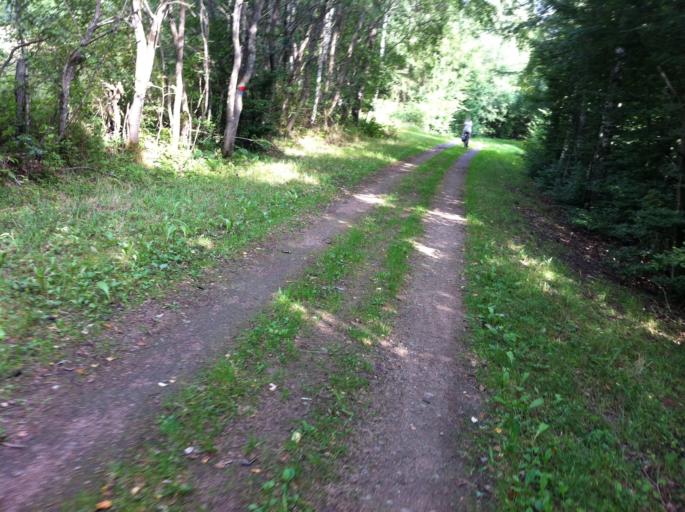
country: SE
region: Skane
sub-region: Hassleholms Kommun
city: Vinslov
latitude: 55.9411
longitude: 13.8301
